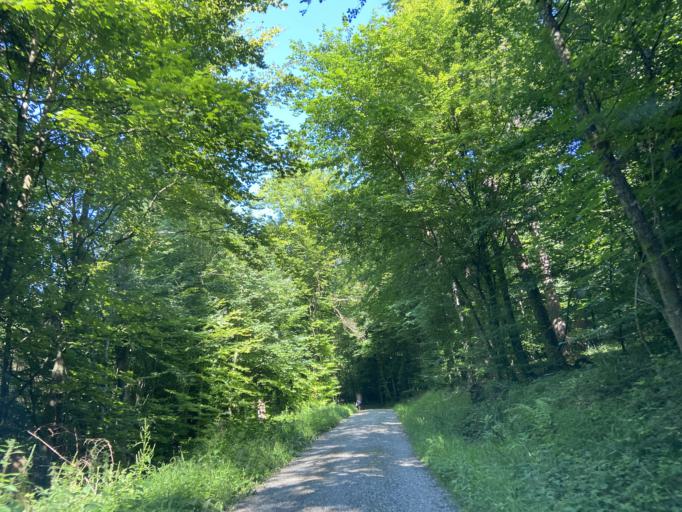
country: CH
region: Zurich
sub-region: Bezirk Winterthur
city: Wuelflingen (Kreis 6) / Niederfeld
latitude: 47.5088
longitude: 8.6616
